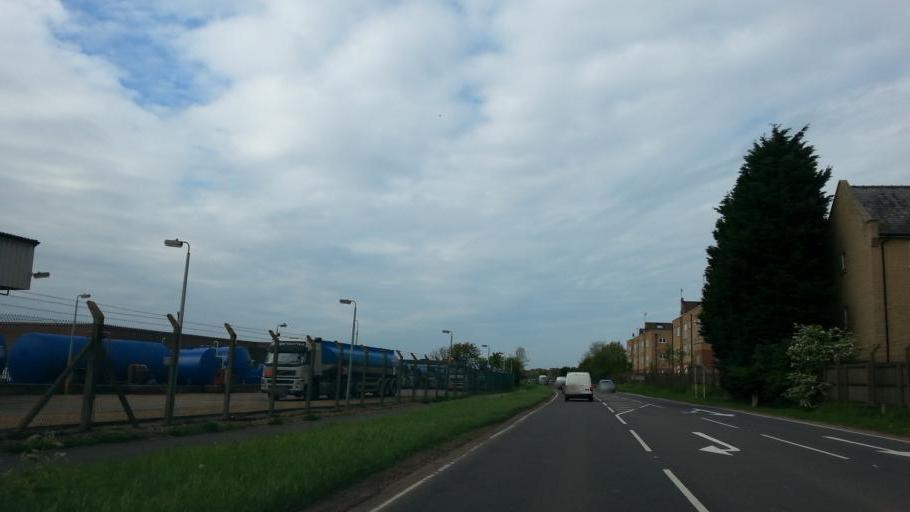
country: GB
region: England
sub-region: Cambridgeshire
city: Chatteris
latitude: 52.4555
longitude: 0.0409
